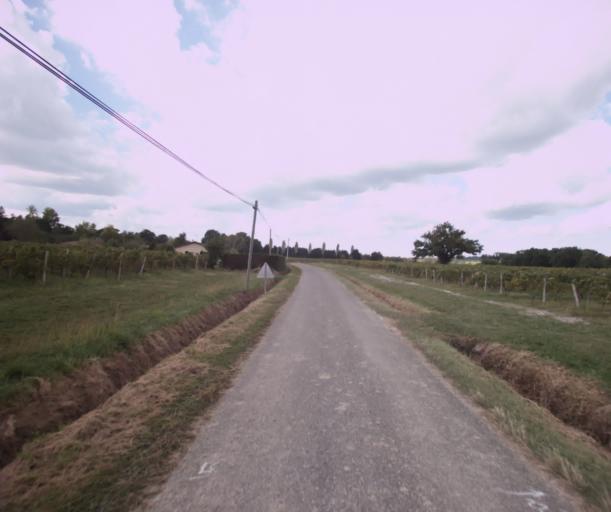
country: FR
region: Midi-Pyrenees
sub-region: Departement du Gers
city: Cazaubon
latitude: 43.8962
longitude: -0.0483
